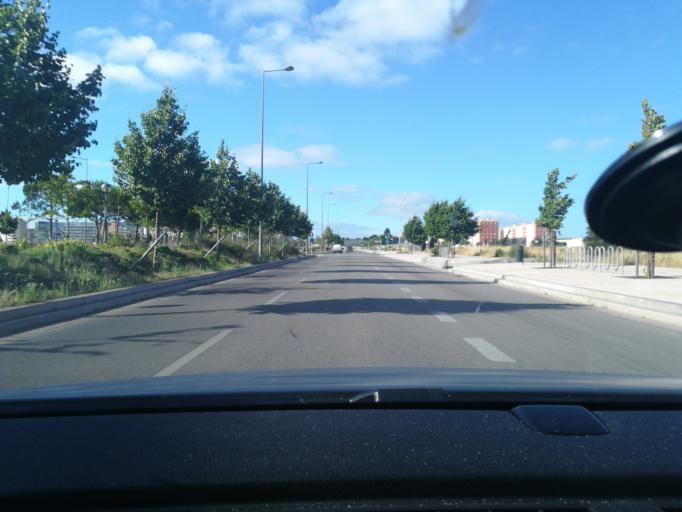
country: PT
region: Lisbon
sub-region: Odivelas
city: Olival do Basto
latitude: 38.7738
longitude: -9.1484
